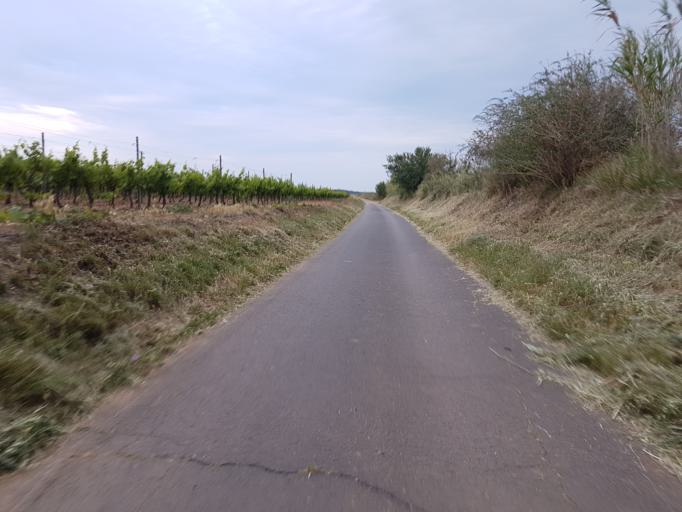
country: FR
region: Languedoc-Roussillon
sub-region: Departement de l'Herault
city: Cers
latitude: 43.3186
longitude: 3.3209
